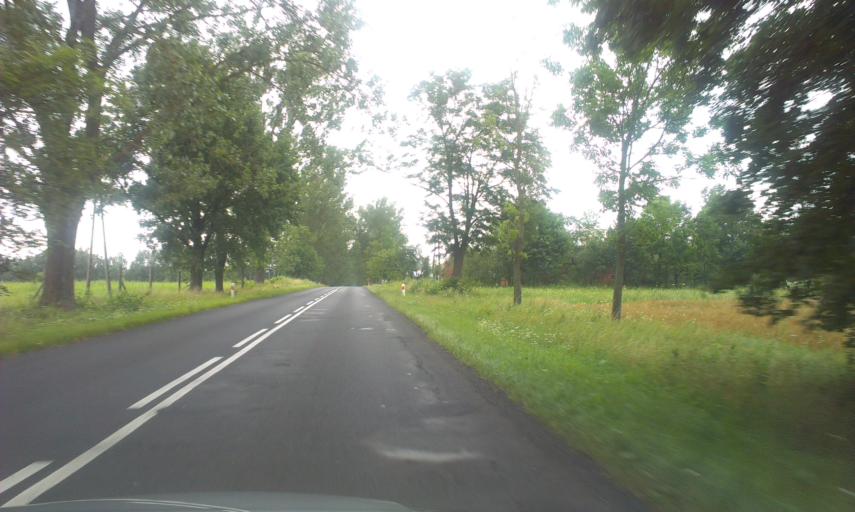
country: PL
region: West Pomeranian Voivodeship
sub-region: Powiat swidwinski
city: Polczyn-Zdroj
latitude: 53.8398
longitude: 16.0763
